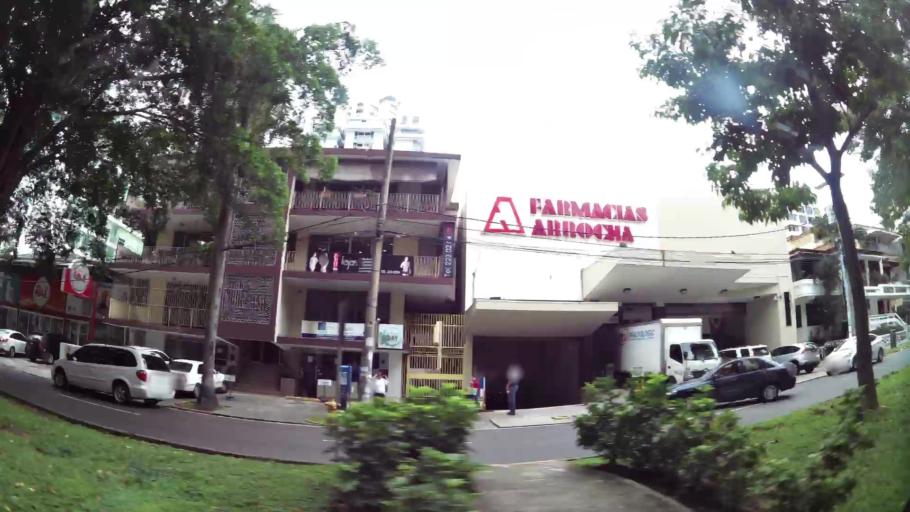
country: PA
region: Panama
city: Panama
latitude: 8.9885
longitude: -79.5287
